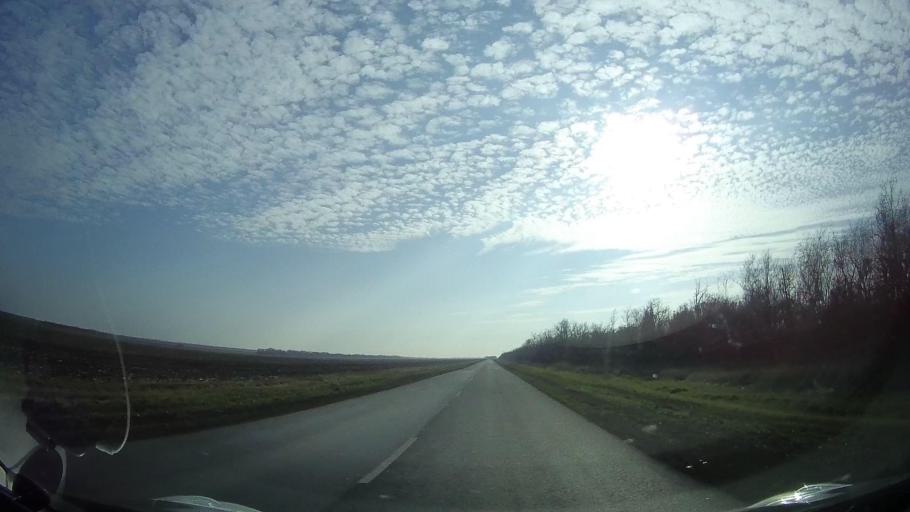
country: RU
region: Rostov
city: Veselyy
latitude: 46.9784
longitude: 40.7200
